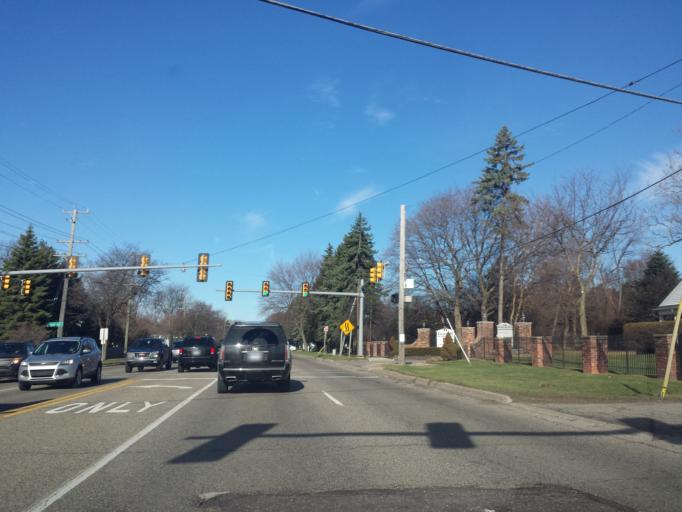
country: US
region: Michigan
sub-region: Oakland County
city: Franklin
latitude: 42.5447
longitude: -83.2880
